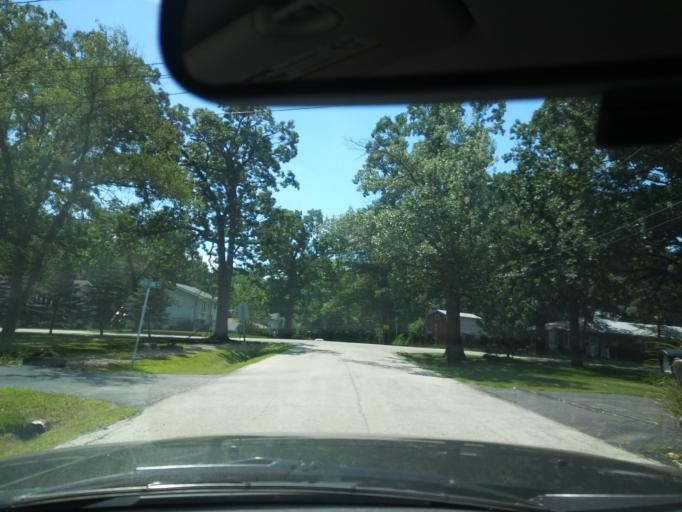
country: US
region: Illinois
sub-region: Cook County
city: Oak Forest
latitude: 41.5980
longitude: -87.7497
